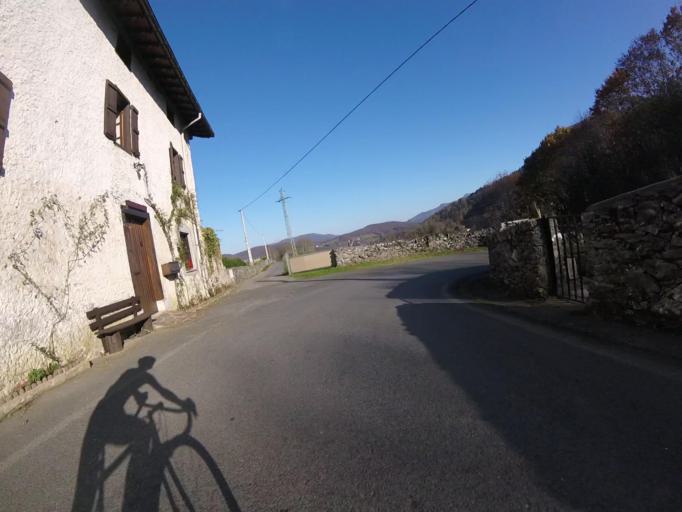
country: ES
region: Navarre
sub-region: Provincia de Navarra
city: Igantzi
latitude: 43.2317
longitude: -1.7037
